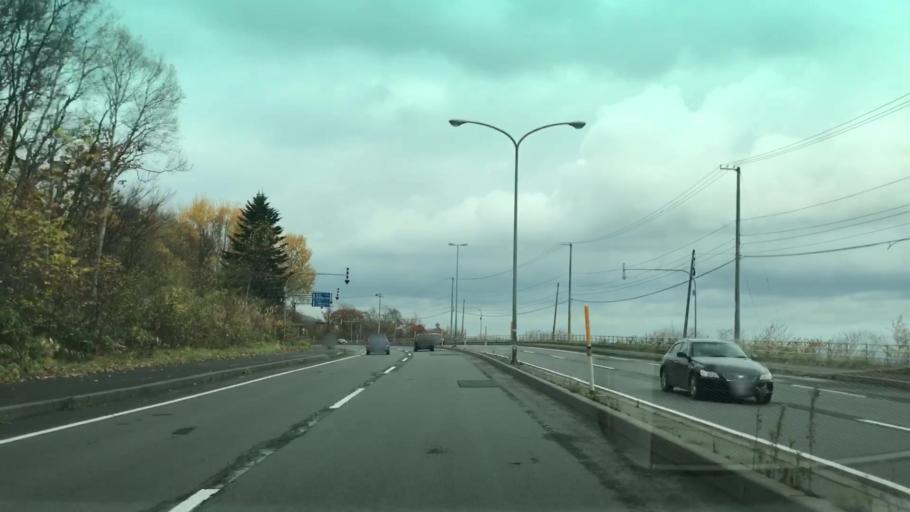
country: JP
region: Hokkaido
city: Otaru
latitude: 43.1609
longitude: 141.1085
